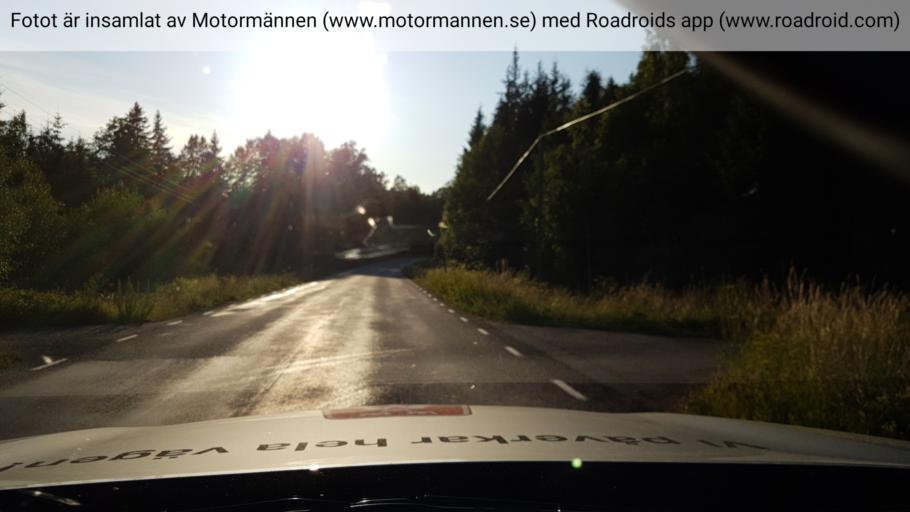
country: SE
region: Vaestmanland
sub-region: Norbergs Kommun
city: Norberg
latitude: 60.0281
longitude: 15.9997
